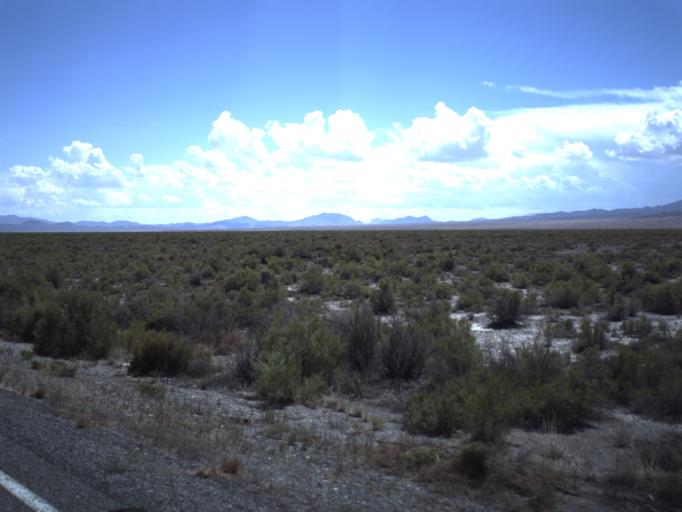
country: US
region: Nevada
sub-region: White Pine County
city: McGill
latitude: 39.0475
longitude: -113.9237
